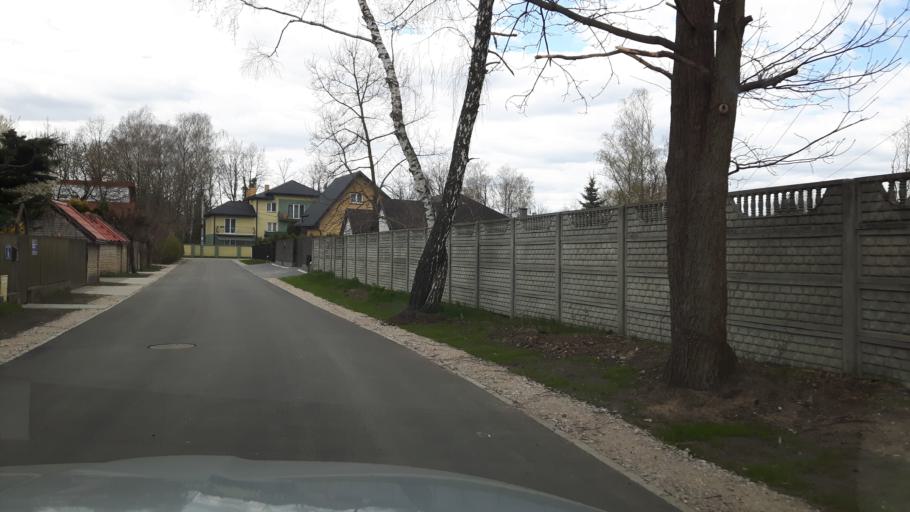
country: PL
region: Masovian Voivodeship
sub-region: Powiat wolominski
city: Kobylka
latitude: 52.3514
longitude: 21.2139
